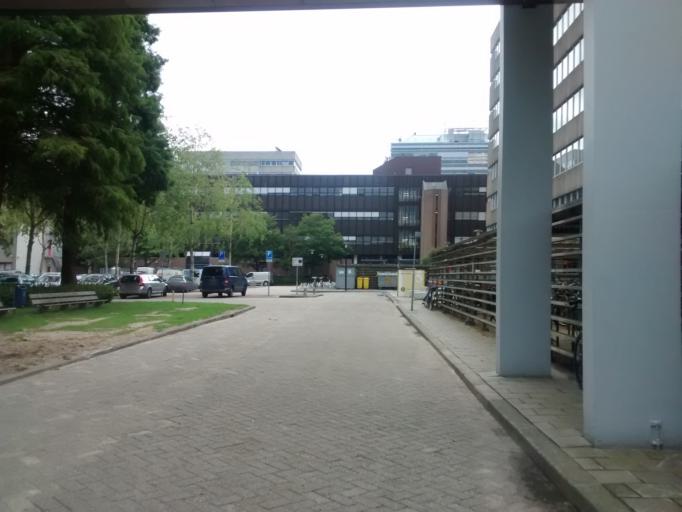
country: NL
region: Utrecht
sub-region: Gemeente De Bilt
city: De Bilt
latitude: 52.0874
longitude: 5.1648
